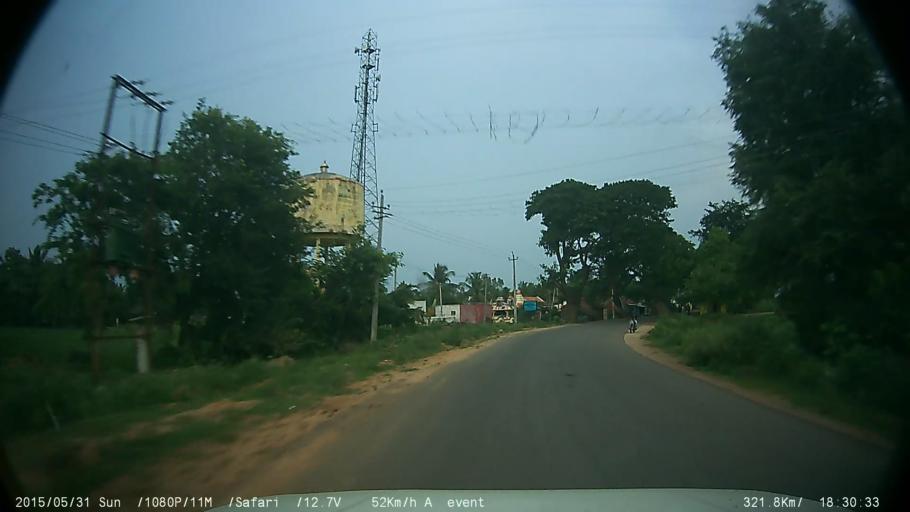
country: IN
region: Karnataka
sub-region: Mysore
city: Nanjangud
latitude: 12.1264
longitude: 76.7388
